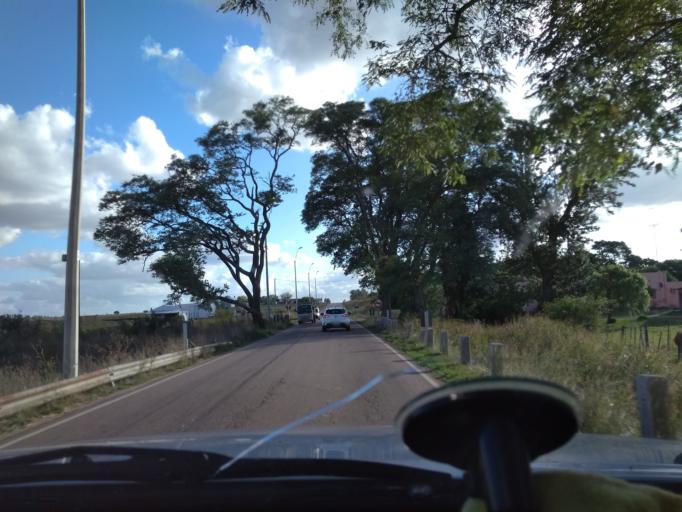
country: UY
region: Canelones
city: Tala
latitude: -34.3655
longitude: -55.7797
